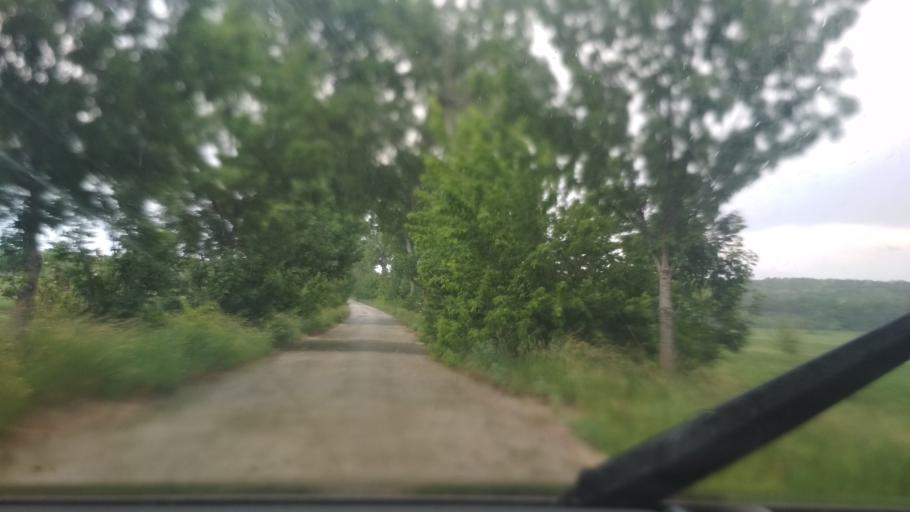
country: MD
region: Singerei
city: Biruinta
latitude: 47.7446
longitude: 28.1382
